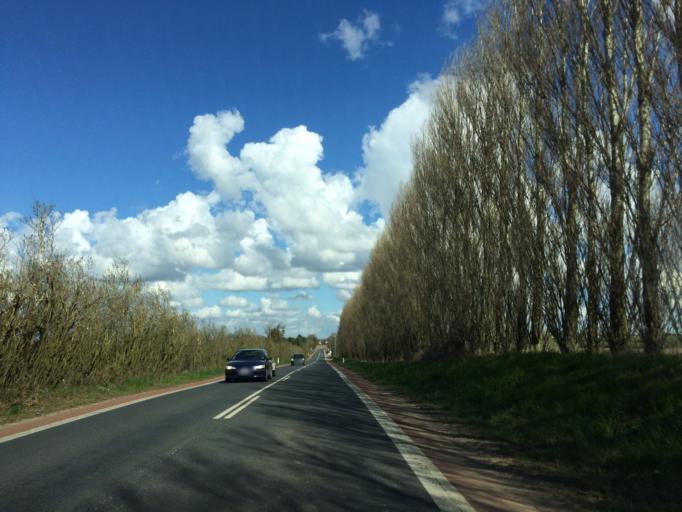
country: DK
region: South Denmark
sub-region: Assens Kommune
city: Harby
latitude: 55.1881
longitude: 10.1531
